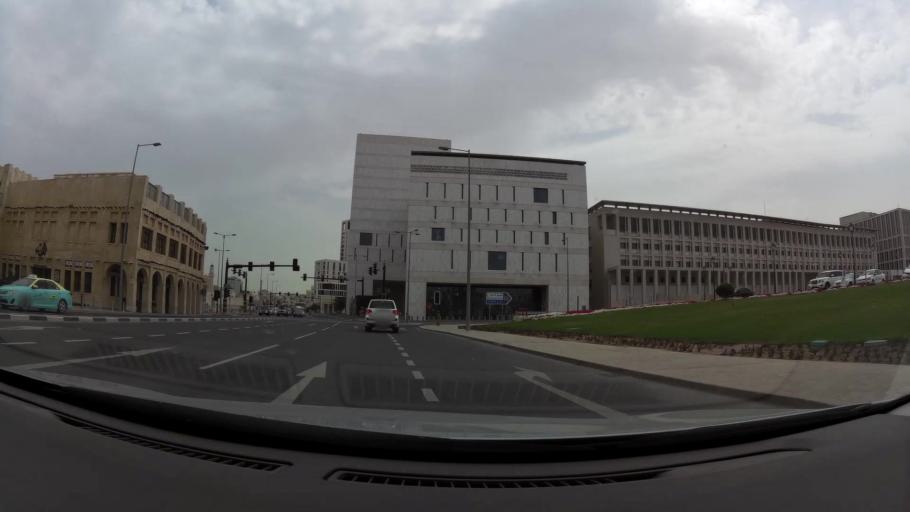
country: QA
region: Baladiyat ad Dawhah
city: Doha
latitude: 25.2888
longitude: 51.5298
